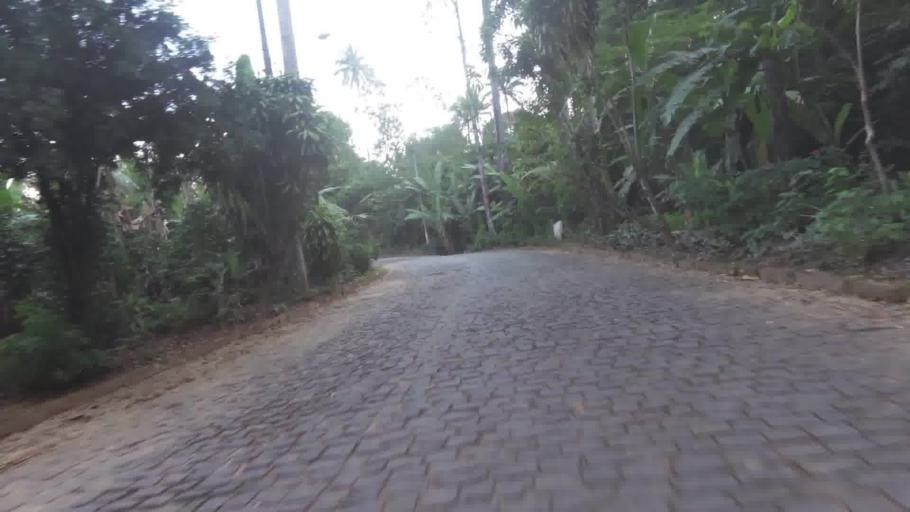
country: BR
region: Espirito Santo
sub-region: Alfredo Chaves
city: Alfredo Chaves
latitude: -20.5825
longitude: -40.6988
